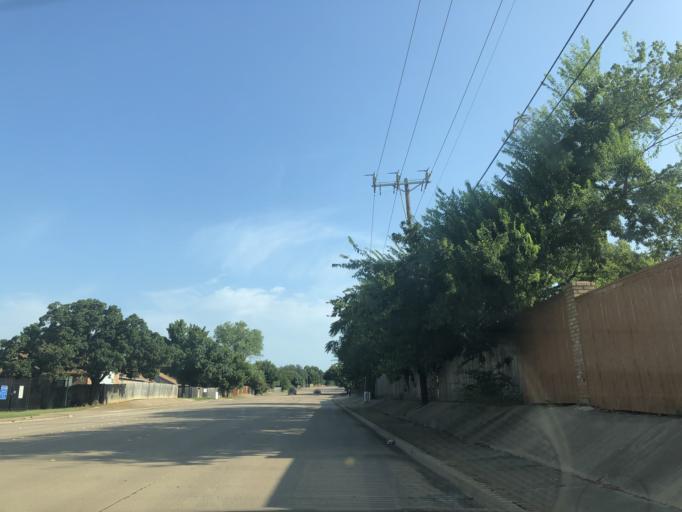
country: US
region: Texas
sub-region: Tarrant County
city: Euless
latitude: 32.8732
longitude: -97.0830
